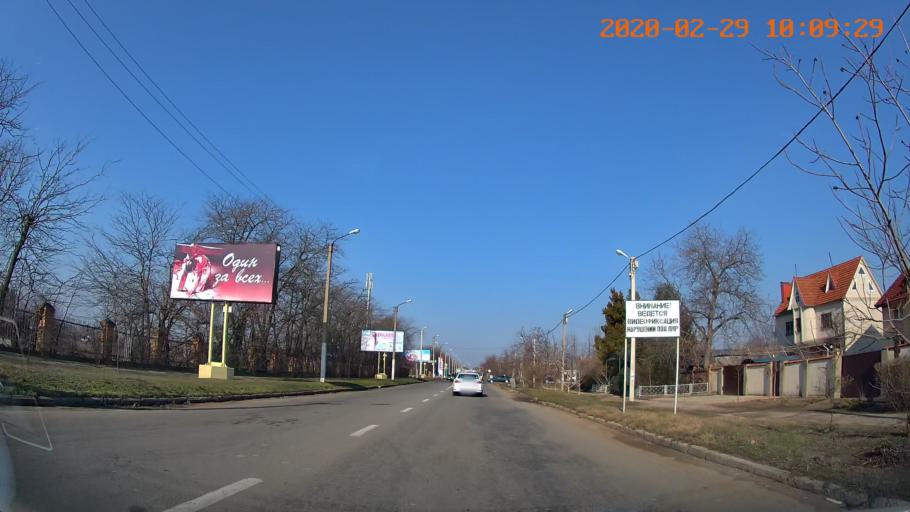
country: MD
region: Telenesti
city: Tiraspolul Nou
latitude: 46.8284
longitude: 29.6519
